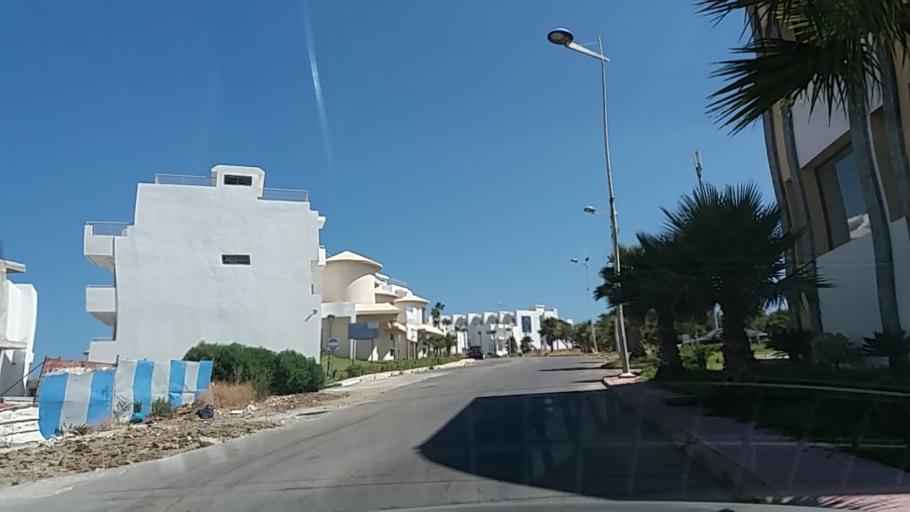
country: MA
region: Tanger-Tetouan
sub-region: Tanger-Assilah
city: Tangier
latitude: 35.7904
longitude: -5.7554
